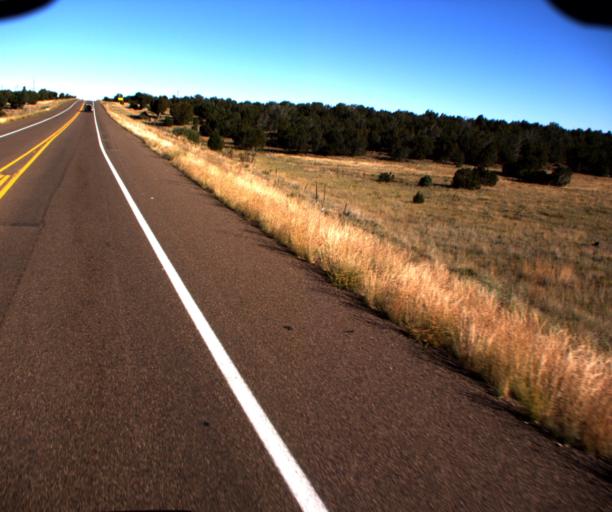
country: US
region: Arizona
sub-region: Navajo County
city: Show Low
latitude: 34.2705
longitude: -110.0232
